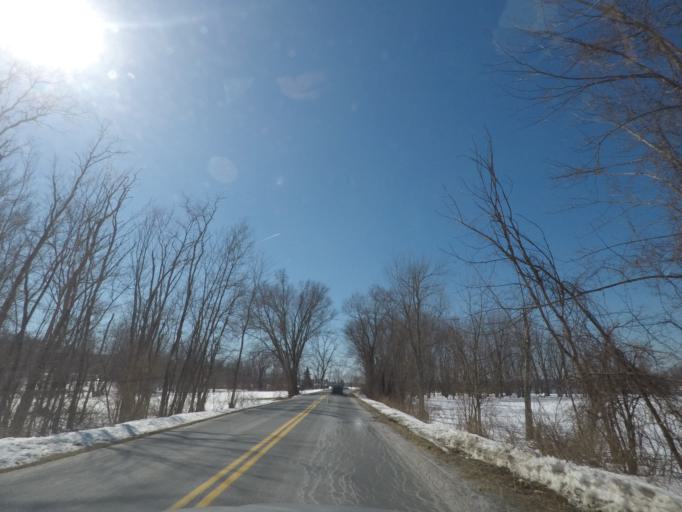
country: US
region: New York
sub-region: Saratoga County
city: Stillwater
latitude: 42.9406
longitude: -73.6330
